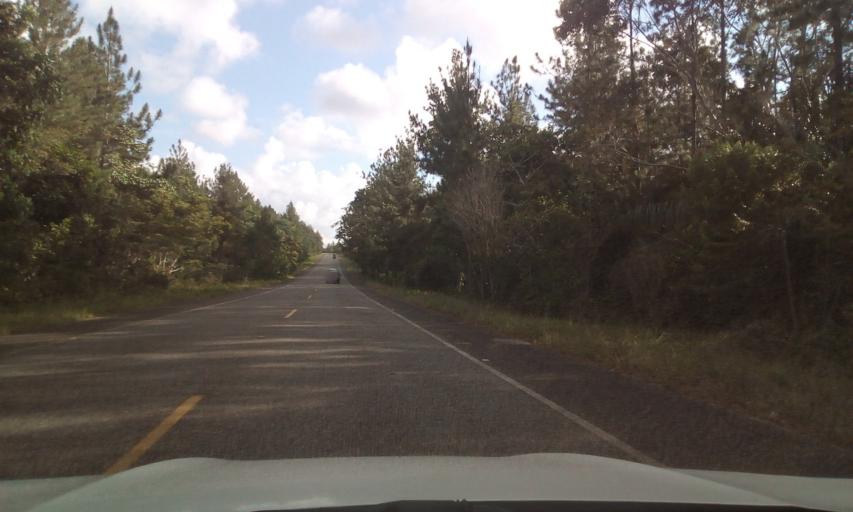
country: BR
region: Bahia
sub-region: Entre Rios
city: Entre Rios
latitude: -12.1474
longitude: -37.7967
